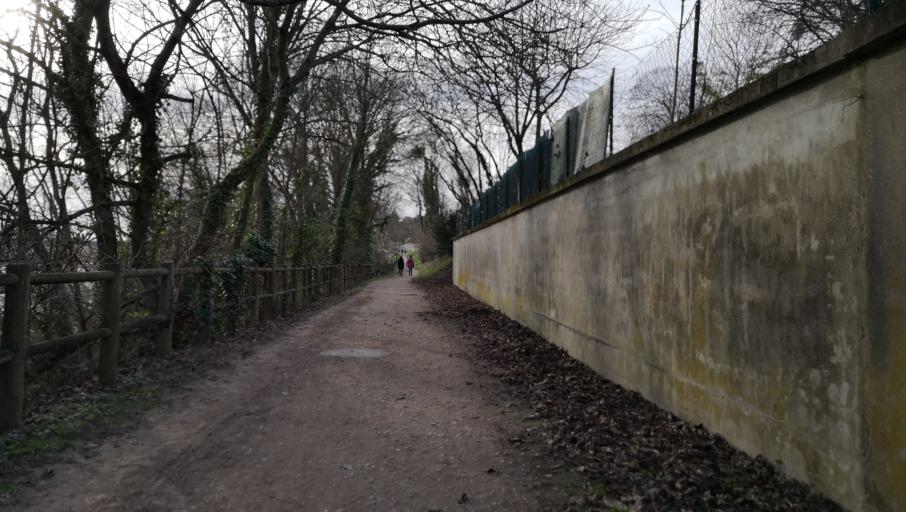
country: FR
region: Centre
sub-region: Departement du Loiret
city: Saint-Pryve-Saint-Mesmin
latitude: 47.8944
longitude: 1.8596
